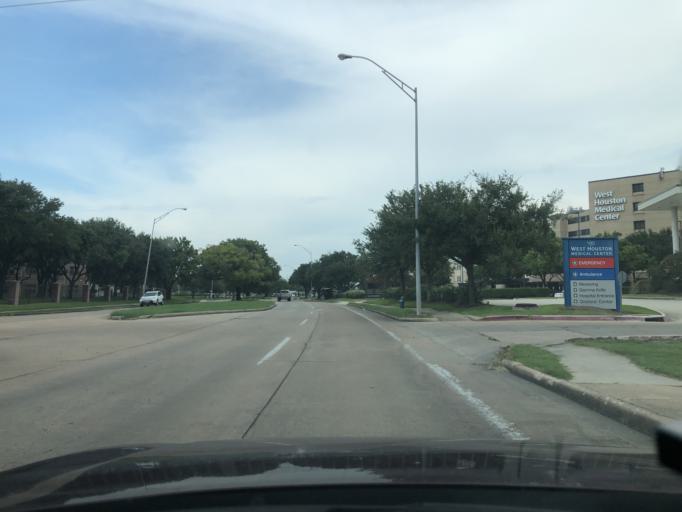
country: US
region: Texas
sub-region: Harris County
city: Bunker Hill Village
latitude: 29.7298
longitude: -95.5964
